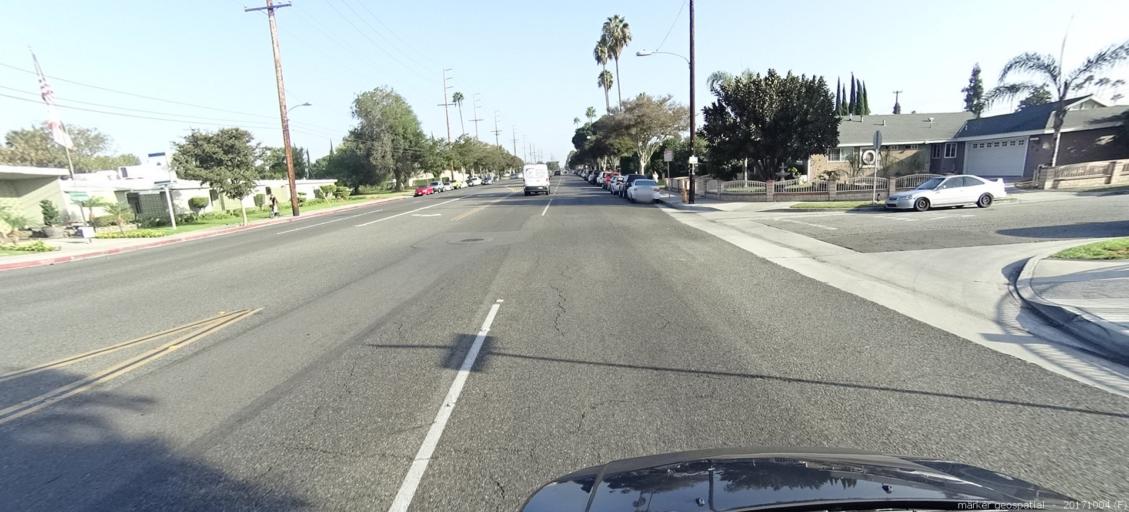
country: US
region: California
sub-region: Orange County
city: Garden Grove
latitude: 33.7782
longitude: -117.9061
